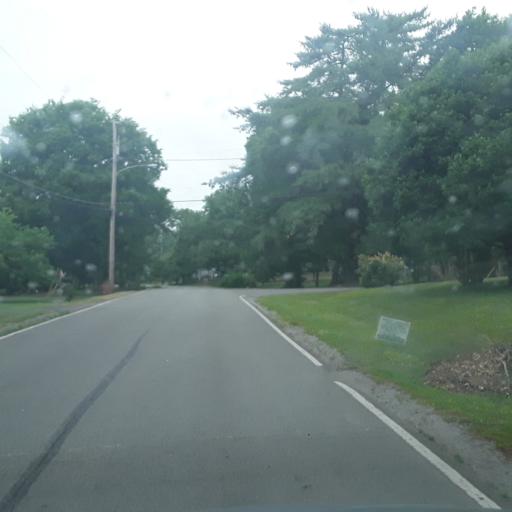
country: US
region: Tennessee
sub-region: Davidson County
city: Oak Hill
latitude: 36.0677
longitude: -86.7550
